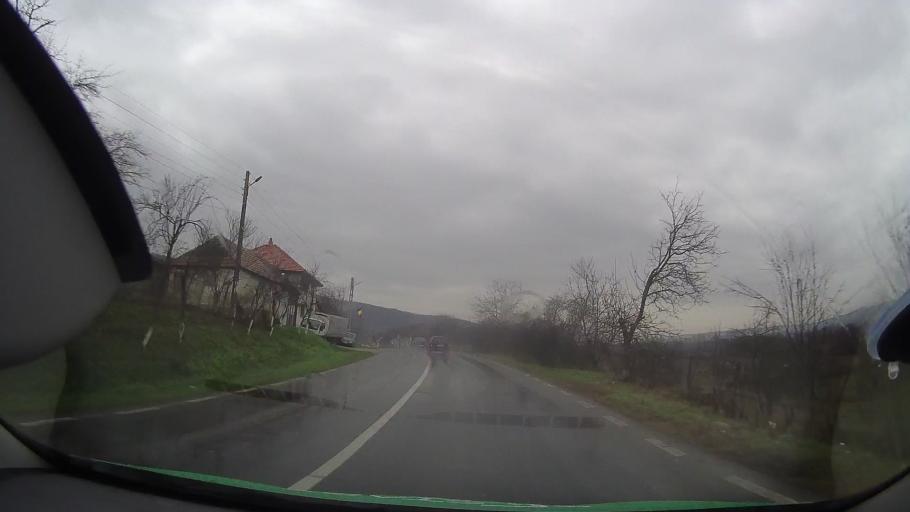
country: RO
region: Bihor
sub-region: Comuna Rabagani
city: Rabagani
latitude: 46.7584
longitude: 22.2009
